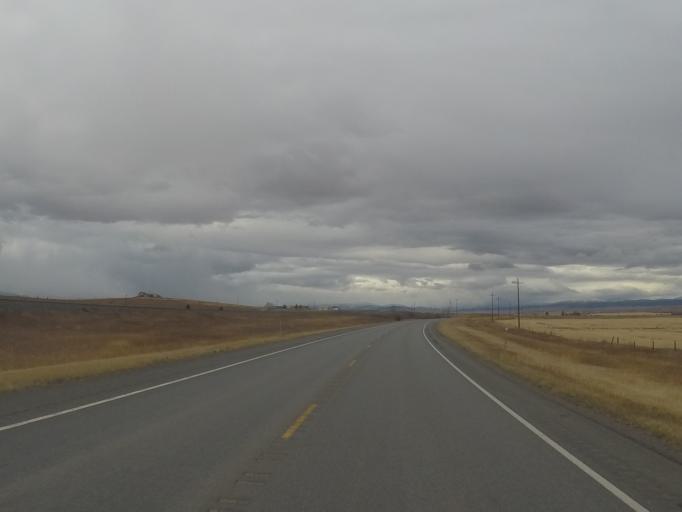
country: US
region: Montana
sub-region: Lewis and Clark County
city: East Helena
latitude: 46.5526
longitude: -111.7672
